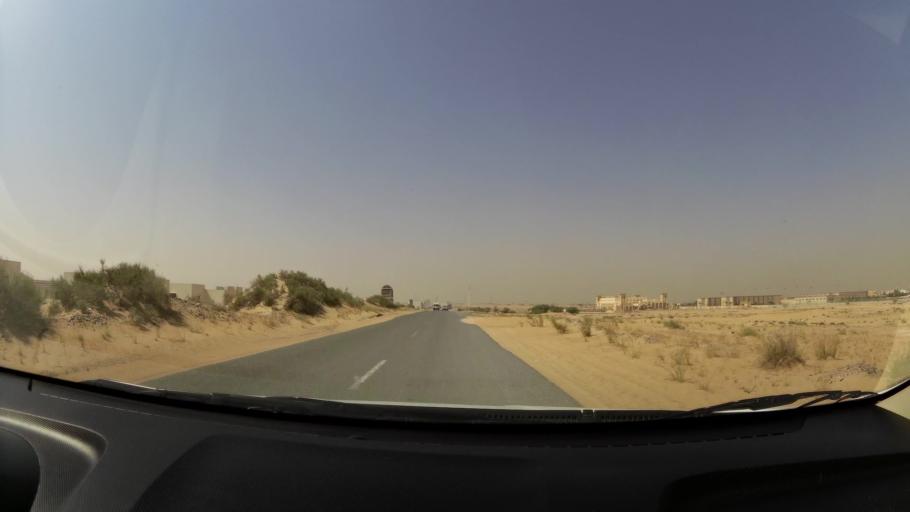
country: AE
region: Ajman
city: Ajman
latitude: 25.3934
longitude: 55.5548
